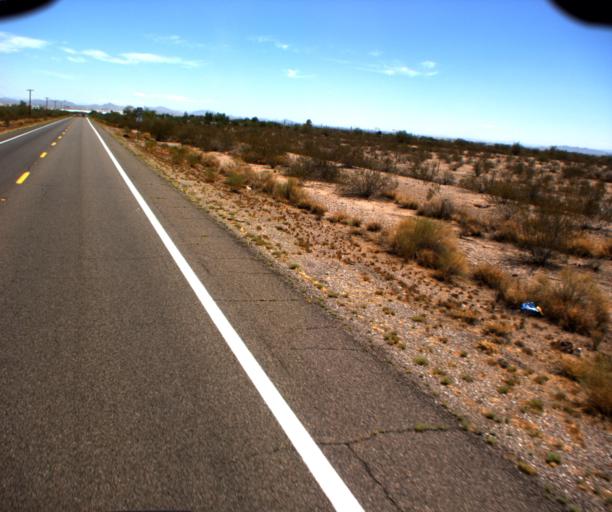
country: US
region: Arizona
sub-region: Pinal County
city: Maricopa
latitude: 32.8707
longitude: -112.0569
